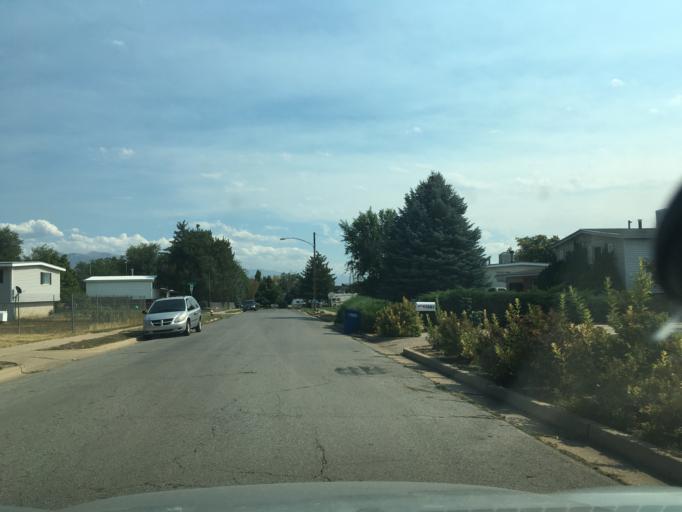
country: US
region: Utah
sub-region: Davis County
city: Clearfield
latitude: 41.0845
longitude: -112.0053
